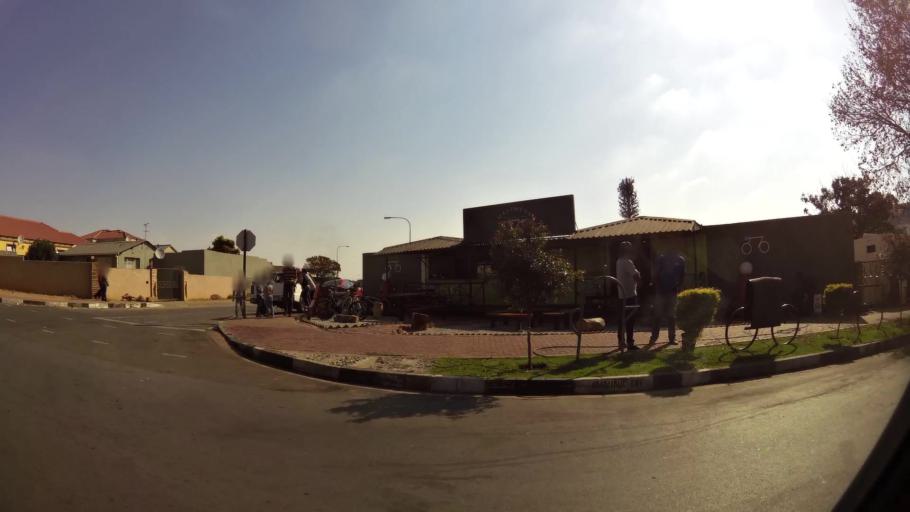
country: ZA
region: Gauteng
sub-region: City of Johannesburg Metropolitan Municipality
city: Johannesburg
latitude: -26.2352
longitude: 27.9522
